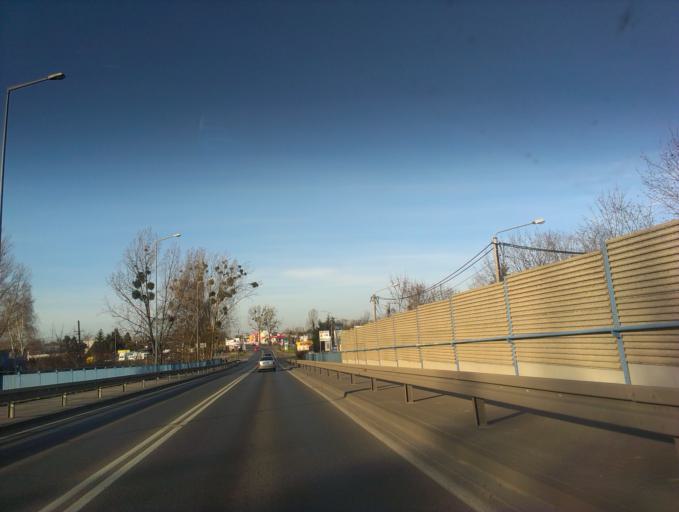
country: PL
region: Greater Poland Voivodeship
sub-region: Powiat poznanski
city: Suchy Las
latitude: 52.4661
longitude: 16.8871
